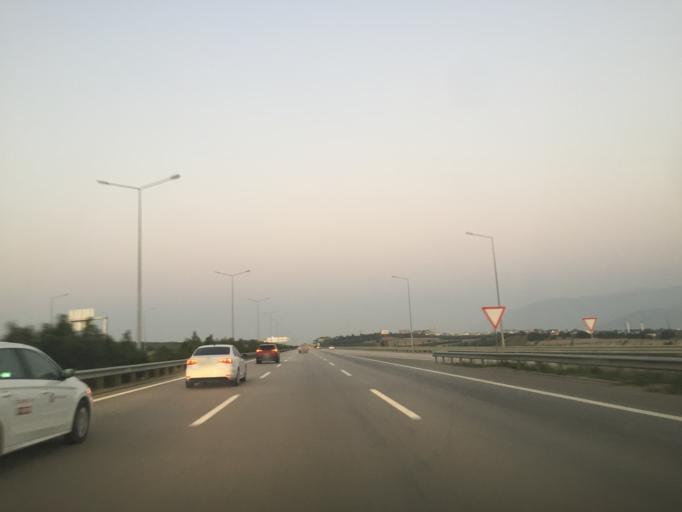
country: TR
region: Bursa
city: Niluefer
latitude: 40.2633
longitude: 28.9136
